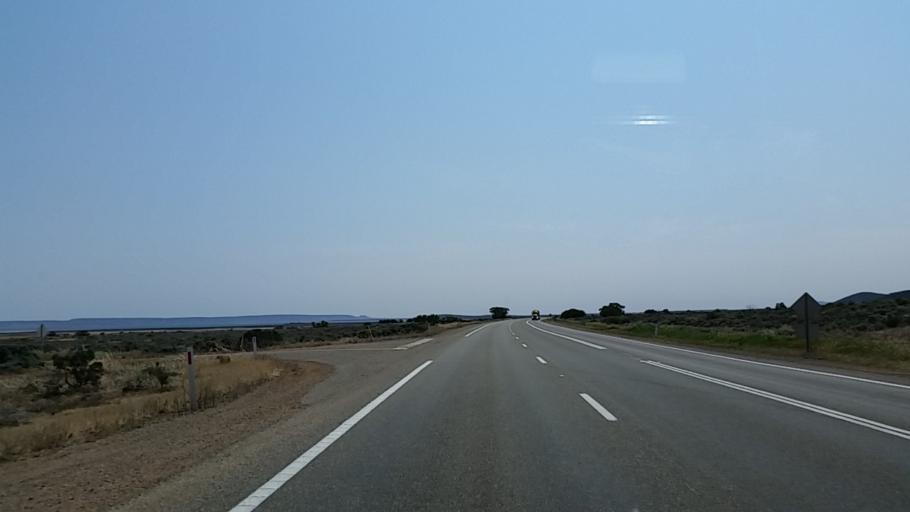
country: AU
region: South Australia
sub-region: Port Augusta
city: Port Augusta
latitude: -32.8061
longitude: 137.9642
